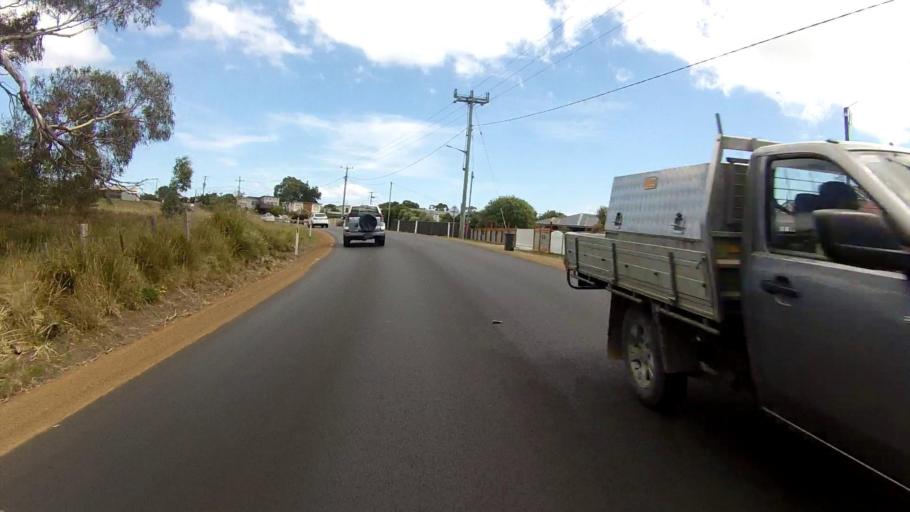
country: AU
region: Tasmania
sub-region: Sorell
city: Sorell
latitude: -42.8506
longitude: 147.6237
